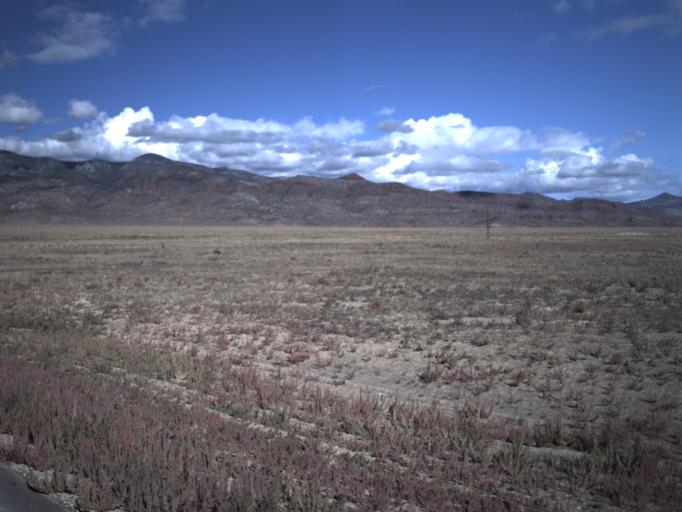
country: US
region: Utah
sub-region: Beaver County
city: Milford
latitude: 38.4827
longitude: -113.4444
